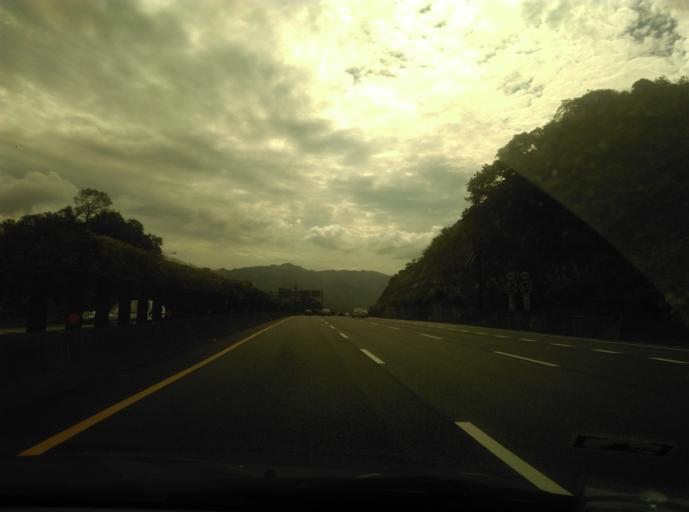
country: TW
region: Taiwan
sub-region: Keelung
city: Keelung
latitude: 25.0917
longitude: 121.6961
